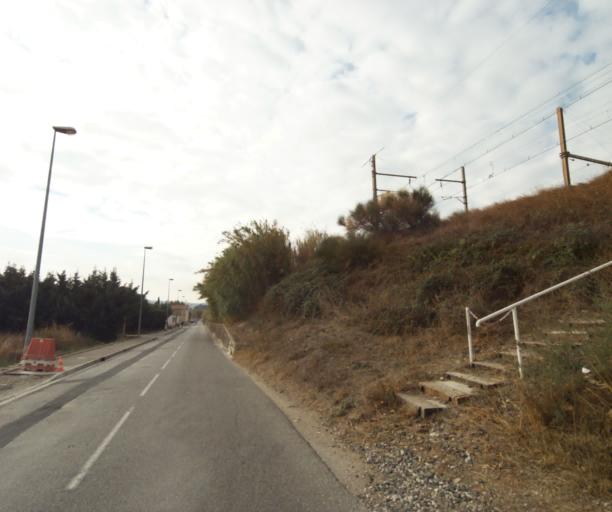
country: FR
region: Provence-Alpes-Cote d'Azur
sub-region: Departement des Bouches-du-Rhone
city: Saint-Victoret
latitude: 43.4167
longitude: 5.2518
